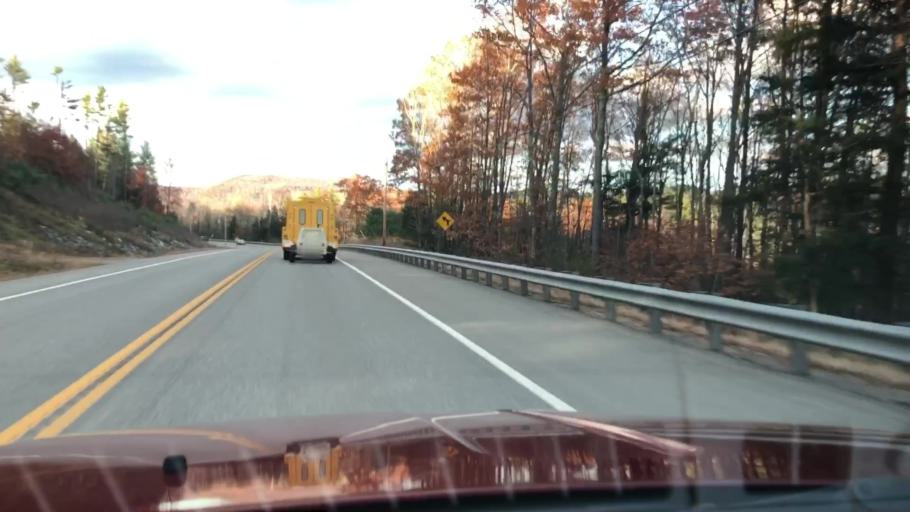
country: US
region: Maine
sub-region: Oxford County
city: Peru
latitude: 44.5292
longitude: -70.4061
